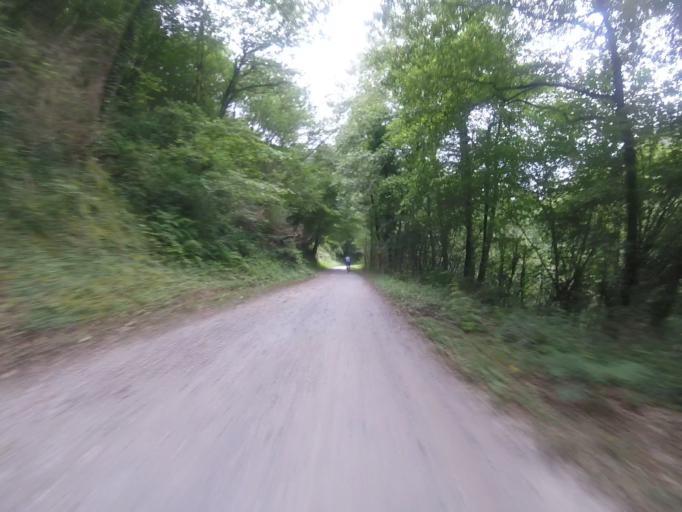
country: ES
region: Navarre
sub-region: Provincia de Navarra
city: Igantzi
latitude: 43.2098
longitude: -1.6674
